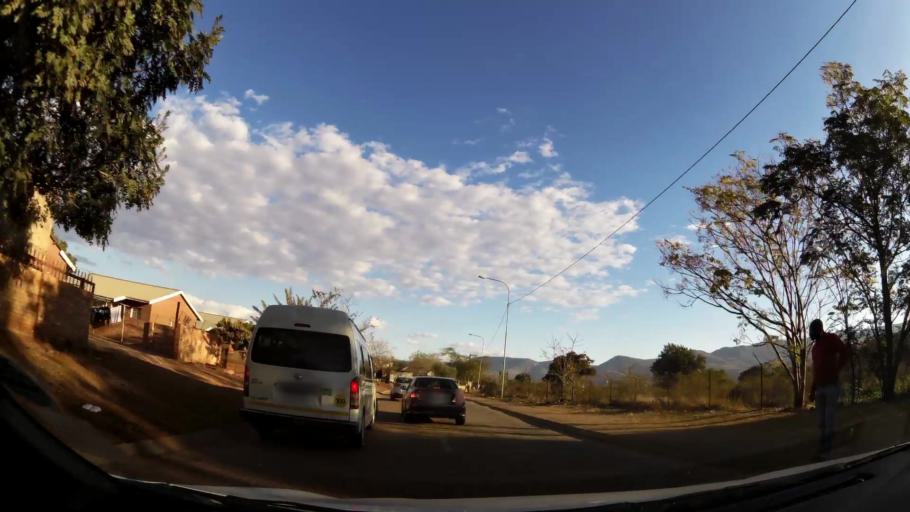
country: ZA
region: Limpopo
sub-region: Waterberg District Municipality
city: Mokopane
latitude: -24.1571
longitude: 28.9886
